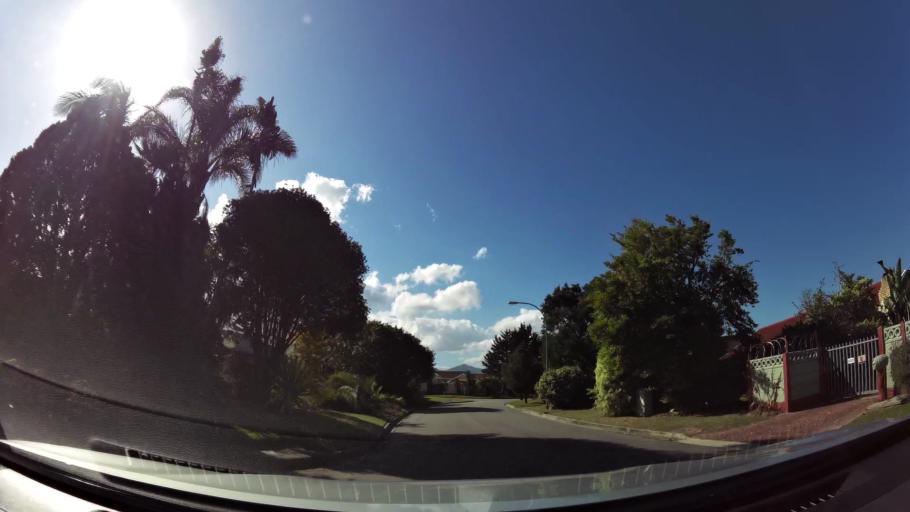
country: ZA
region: Western Cape
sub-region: Eden District Municipality
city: George
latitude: -33.9777
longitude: 22.4436
